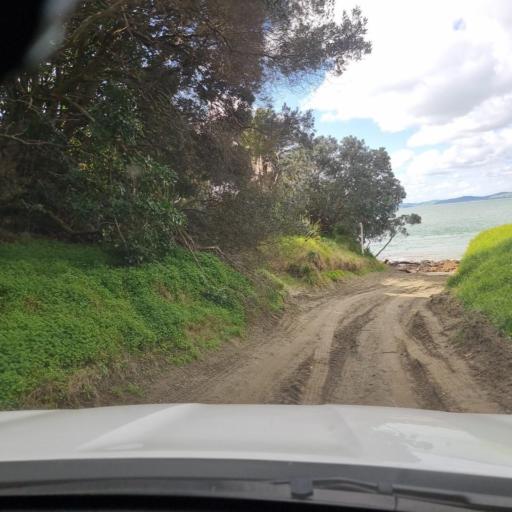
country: NZ
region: Auckland
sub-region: Auckland
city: Wellsford
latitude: -36.3632
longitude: 174.1812
